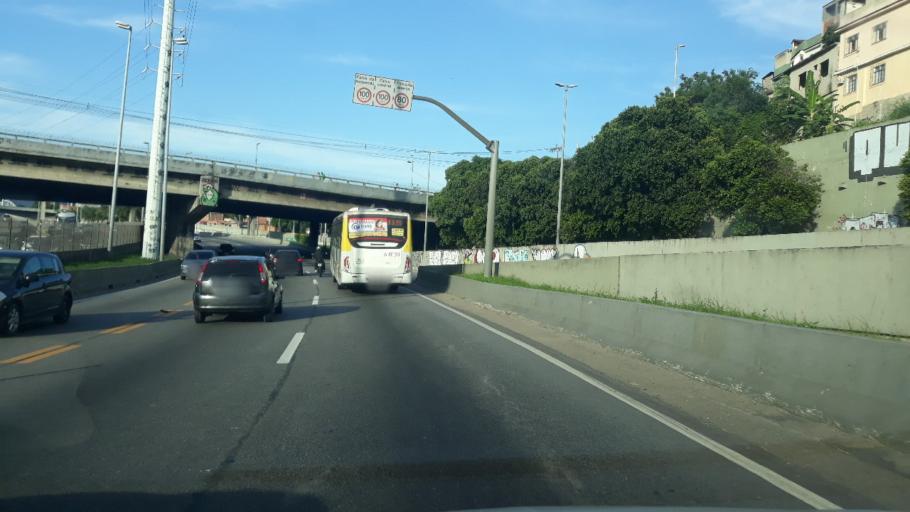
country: BR
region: Rio de Janeiro
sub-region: Rio De Janeiro
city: Rio de Janeiro
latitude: -22.8761
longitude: -43.2751
